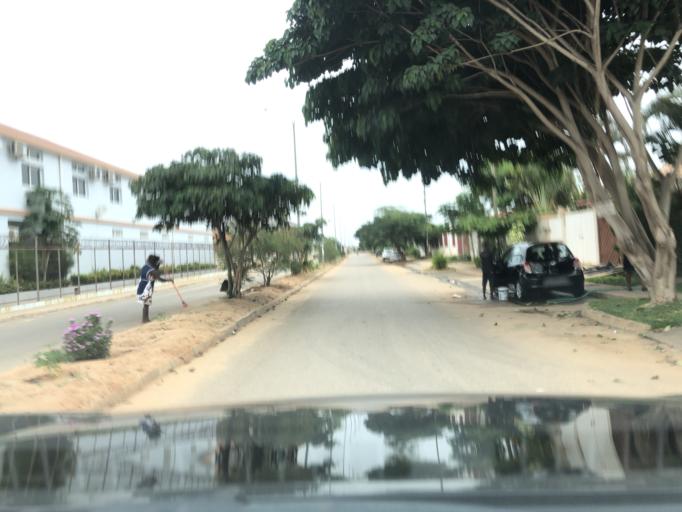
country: AO
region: Luanda
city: Luanda
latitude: -8.9349
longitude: 13.2488
